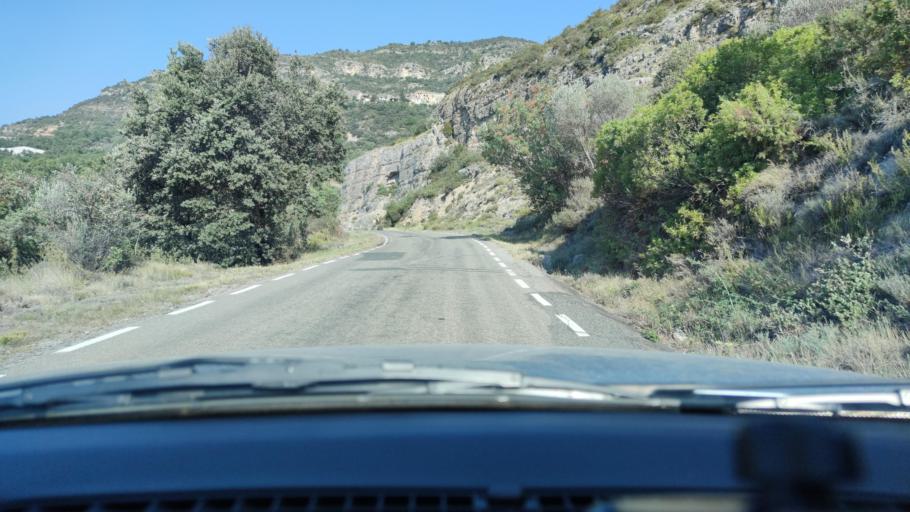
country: ES
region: Catalonia
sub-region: Provincia de Lleida
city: Llimiana
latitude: 42.0846
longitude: 0.8492
